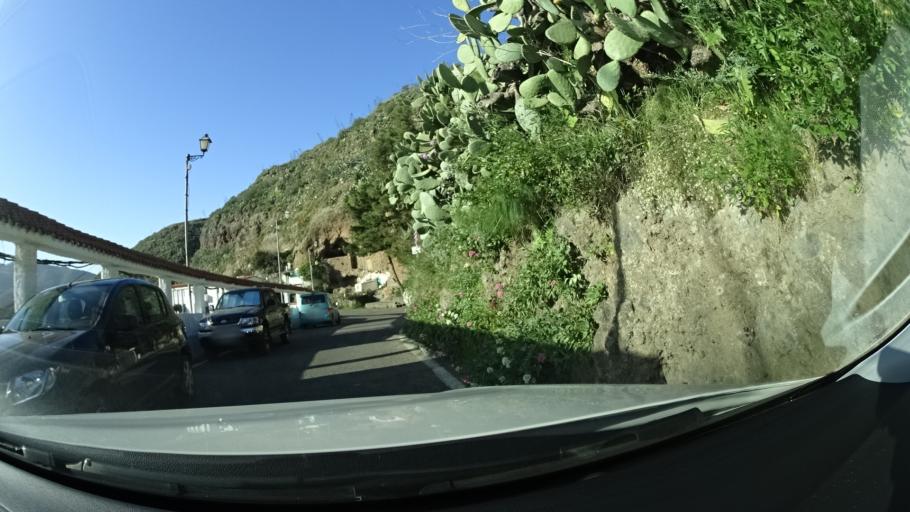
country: ES
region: Canary Islands
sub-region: Provincia de Las Palmas
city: Artenara
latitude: 28.0430
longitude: -15.6524
